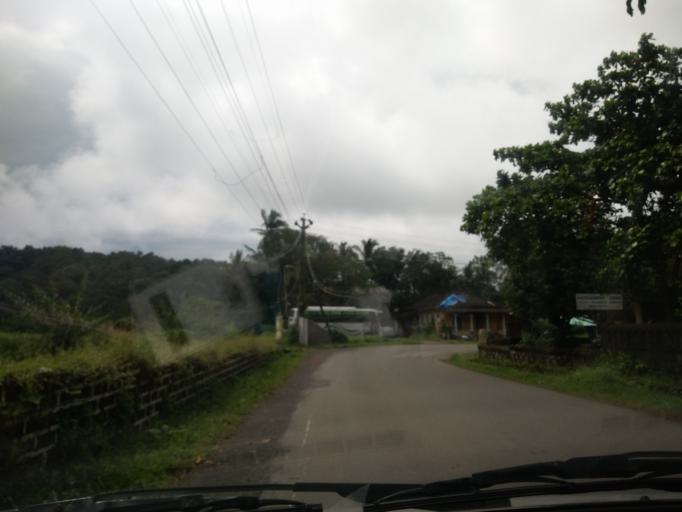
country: IN
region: Goa
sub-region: South Goa
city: Davorlim
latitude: 15.2899
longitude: 74.0210
